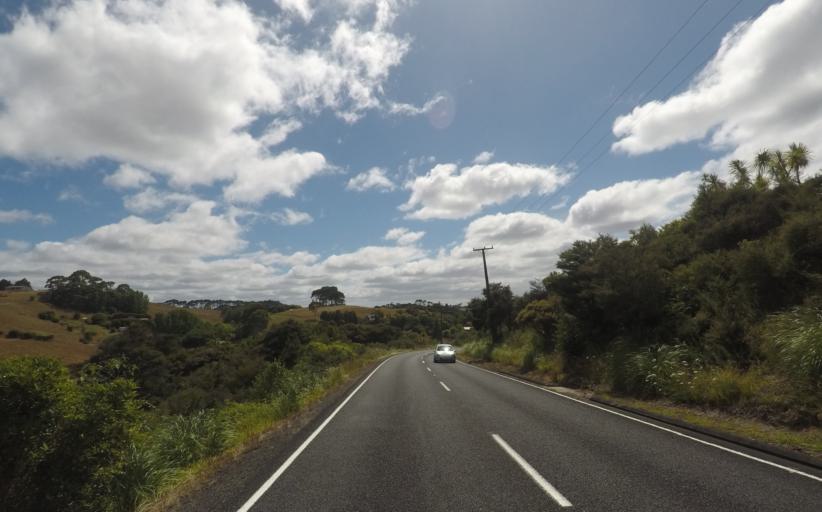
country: NZ
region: Auckland
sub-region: Auckland
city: Muriwai Beach
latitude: -36.8520
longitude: 174.5325
